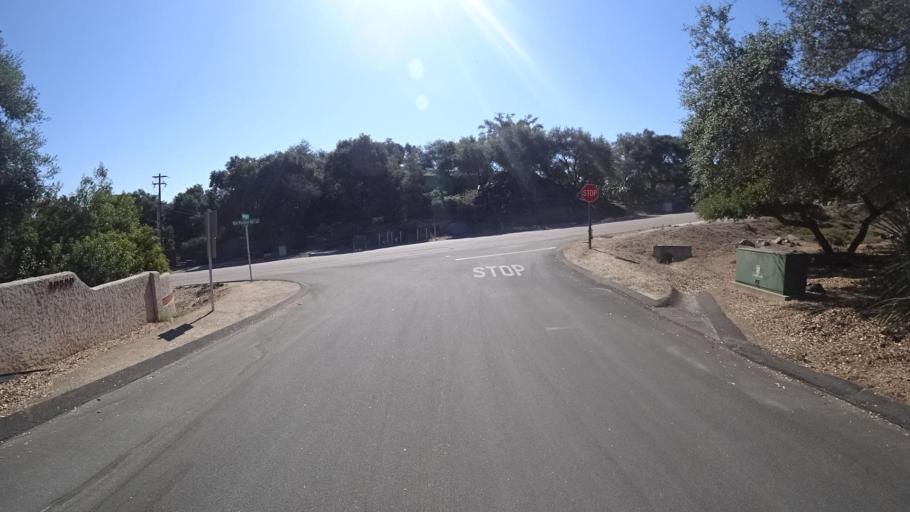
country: US
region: California
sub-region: San Diego County
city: Hidden Meadows
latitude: 33.2082
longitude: -117.1098
